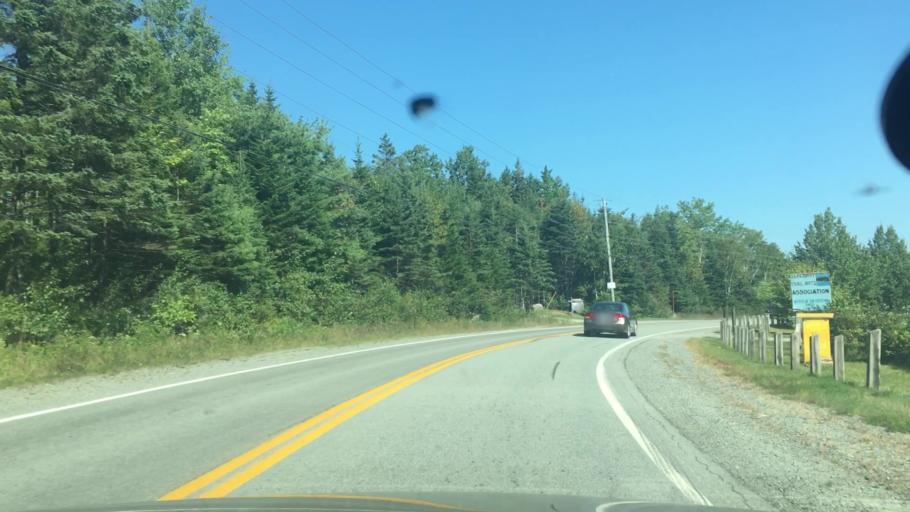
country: CA
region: Nova Scotia
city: New Glasgow
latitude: 44.9268
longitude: -62.5462
